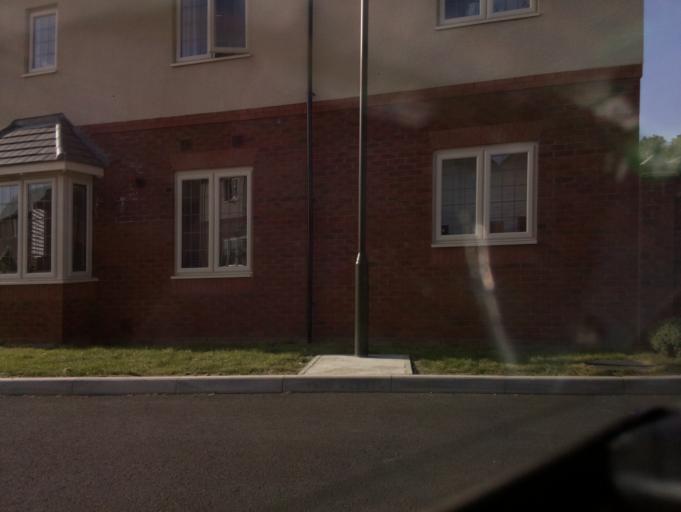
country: GB
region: England
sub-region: Gloucestershire
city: Tewkesbury
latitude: 51.9786
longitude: -2.1453
